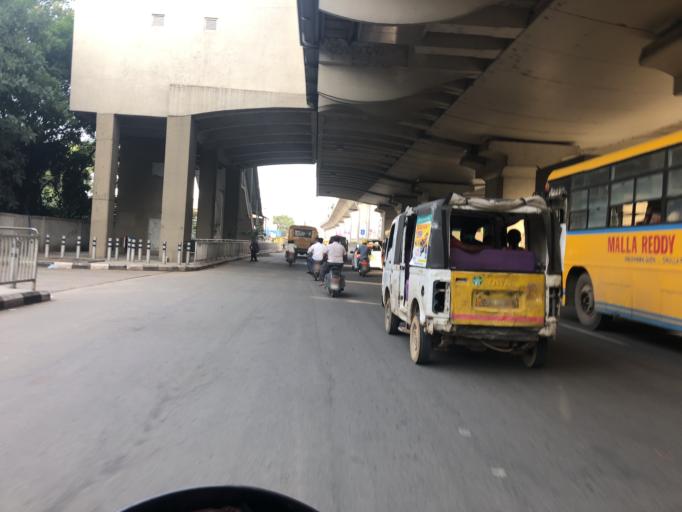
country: IN
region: Telangana
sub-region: Rangareddi
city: Kukatpalli
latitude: 17.4723
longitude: 78.4259
